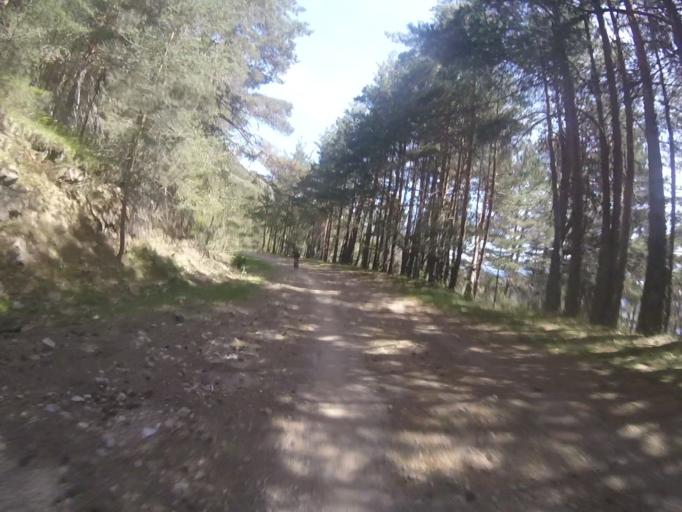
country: ES
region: Madrid
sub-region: Provincia de Madrid
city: Cercedilla
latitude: 40.8016
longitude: -4.0585
